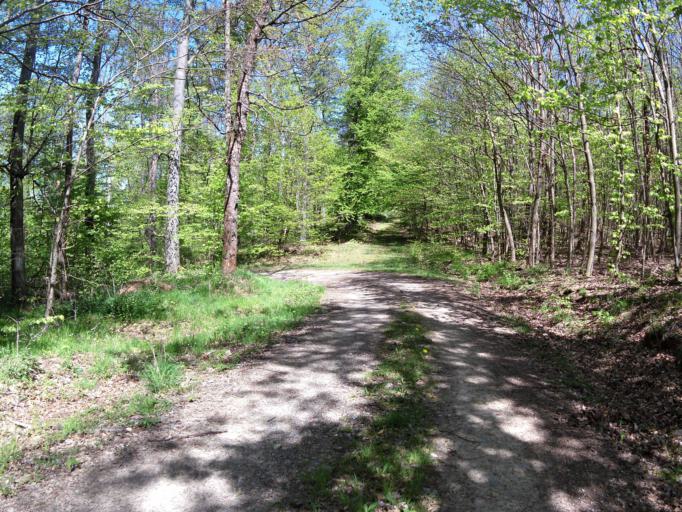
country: DE
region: Thuringia
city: Wolfsburg-Unkeroda
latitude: 50.9663
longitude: 10.2749
